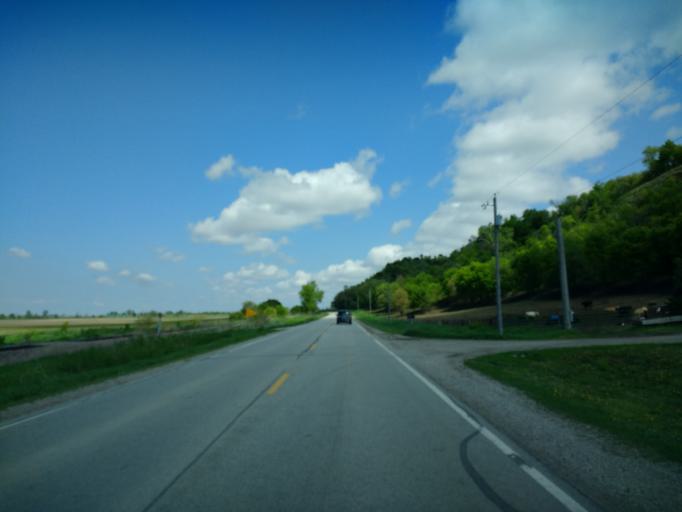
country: US
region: Iowa
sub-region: Harrison County
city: Missouri Valley
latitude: 41.4816
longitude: -95.8843
